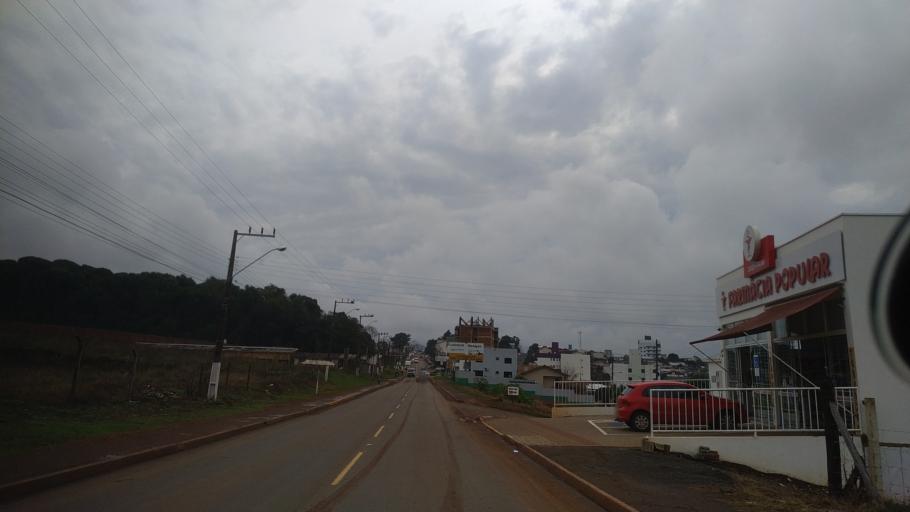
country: BR
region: Santa Catarina
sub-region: Chapeco
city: Chapeco
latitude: -27.1044
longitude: -52.6734
